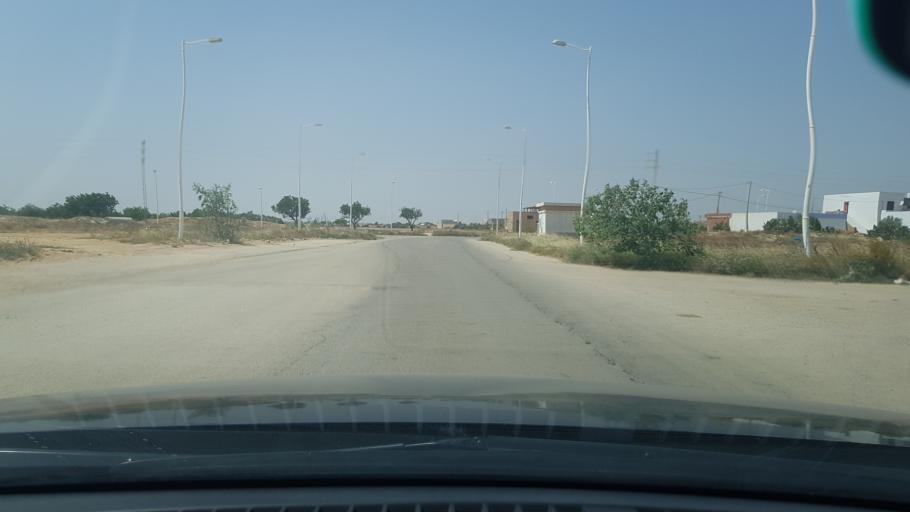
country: TN
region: Safaqis
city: Al Qarmadah
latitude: 34.8336
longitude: 10.7465
